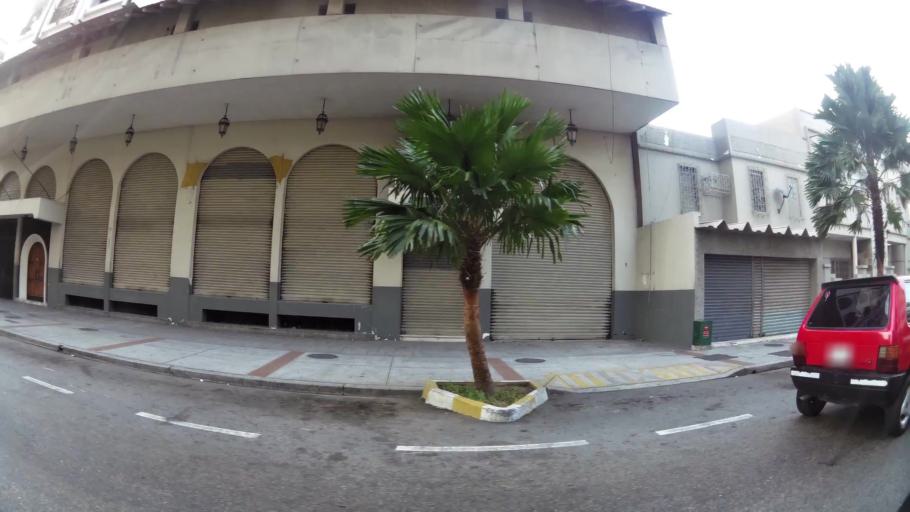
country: EC
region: Guayas
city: Guayaquil
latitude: -2.1884
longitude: -79.8941
